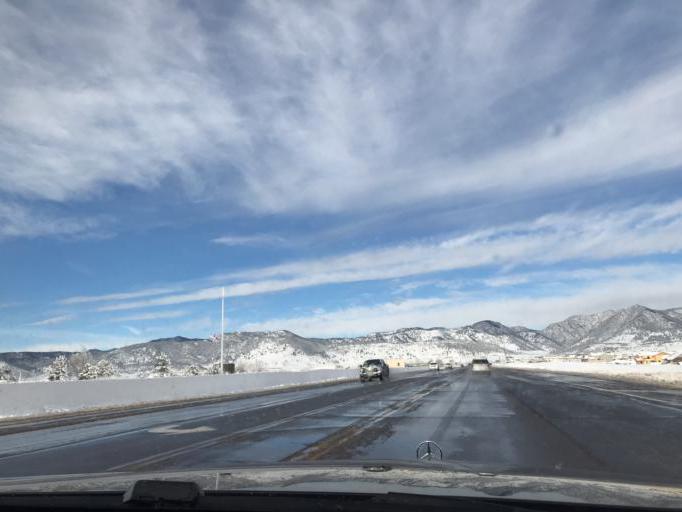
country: US
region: Colorado
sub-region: Boulder County
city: Superior
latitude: 39.8629
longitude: -105.2057
